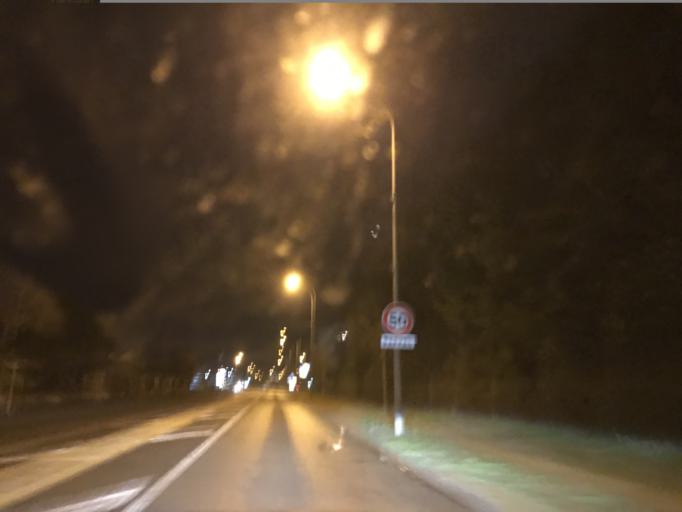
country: FR
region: Auvergne
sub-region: Departement de l'Allier
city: Vichy
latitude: 46.1136
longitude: 3.4190
